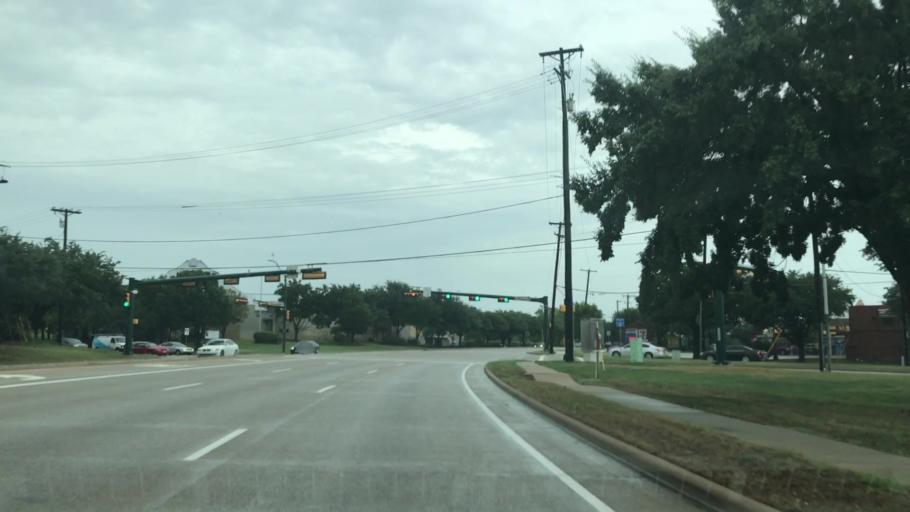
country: US
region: Texas
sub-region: Denton County
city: Highland Village
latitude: 33.0417
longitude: -97.0453
